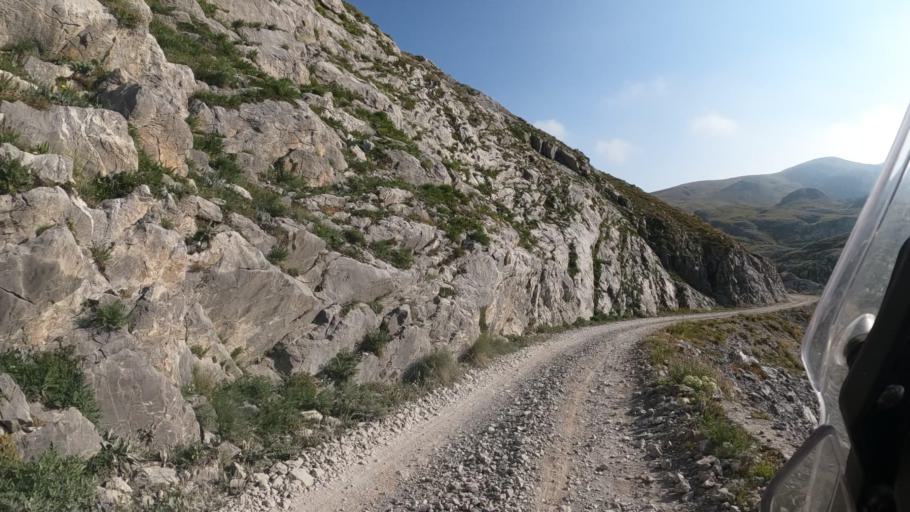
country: IT
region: Piedmont
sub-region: Provincia di Cuneo
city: Limone Piemonte
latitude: 44.1718
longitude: 7.6357
